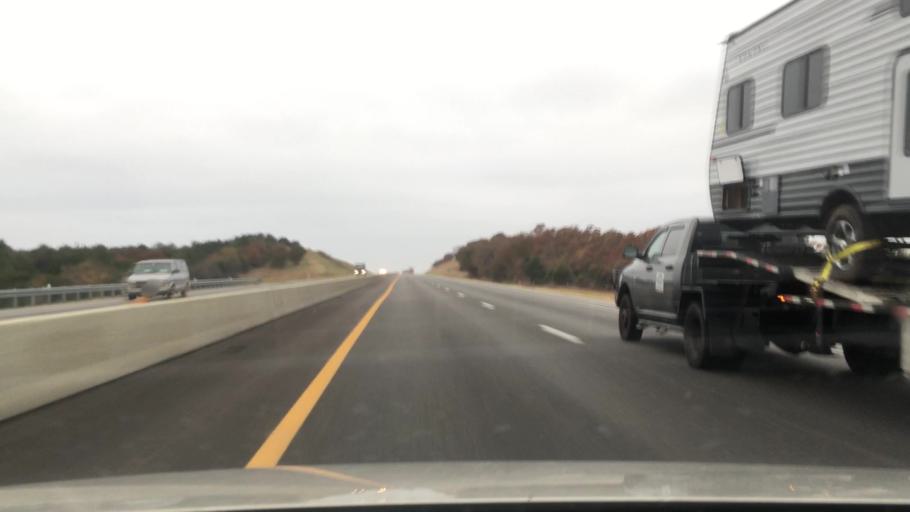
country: US
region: Oklahoma
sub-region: Lincoln County
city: Chandler
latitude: 35.7382
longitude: -96.7785
